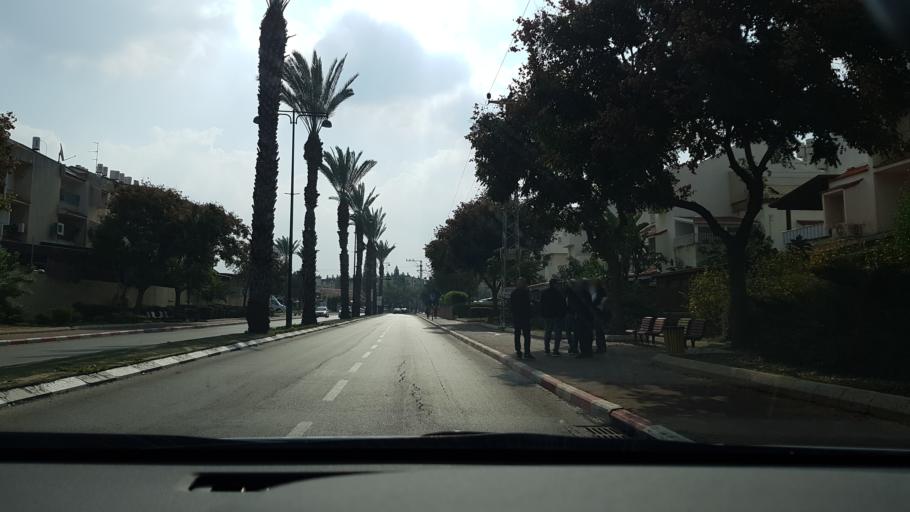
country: IL
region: Central District
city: Mazkeret Batya
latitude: 31.8671
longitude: 34.8200
